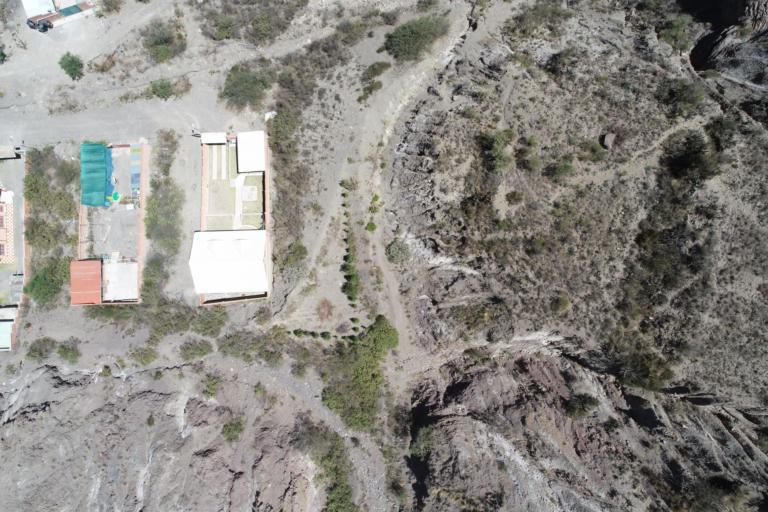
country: BO
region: La Paz
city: La Paz
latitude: -16.6199
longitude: -68.0556
